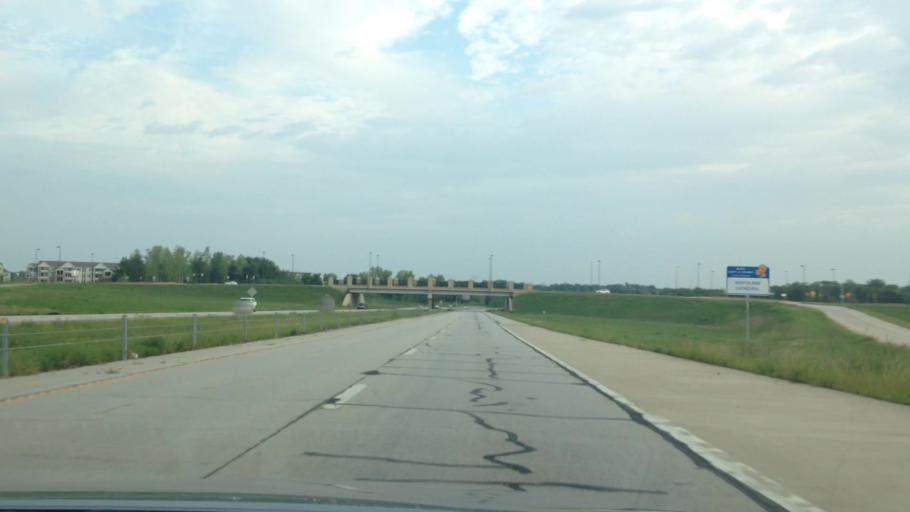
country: US
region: Missouri
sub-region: Clay County
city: Gladstone
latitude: 39.2728
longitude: -94.5850
